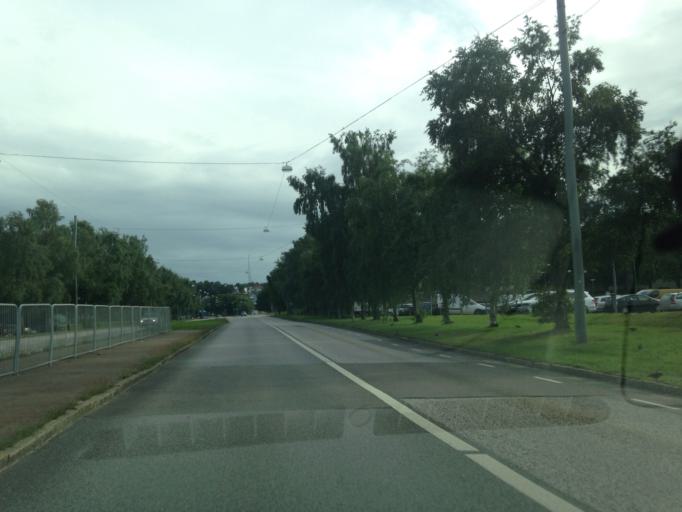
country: SE
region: Vaestra Goetaland
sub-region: Goteborg
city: Goeteborg
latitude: 57.7453
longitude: 11.9767
